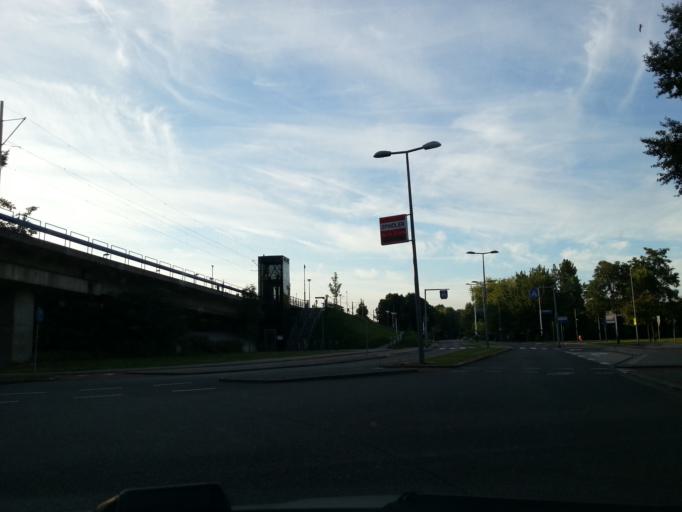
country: NL
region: South Holland
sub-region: Gemeente Rotterdam
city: Rotterdam
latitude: 51.9417
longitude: 4.4608
